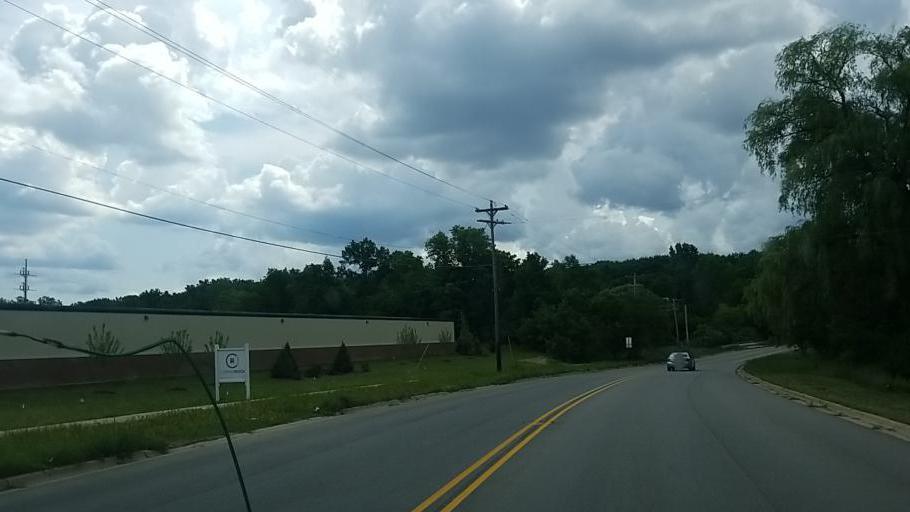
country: US
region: Michigan
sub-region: Kent County
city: Walker
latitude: 43.0017
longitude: -85.7185
